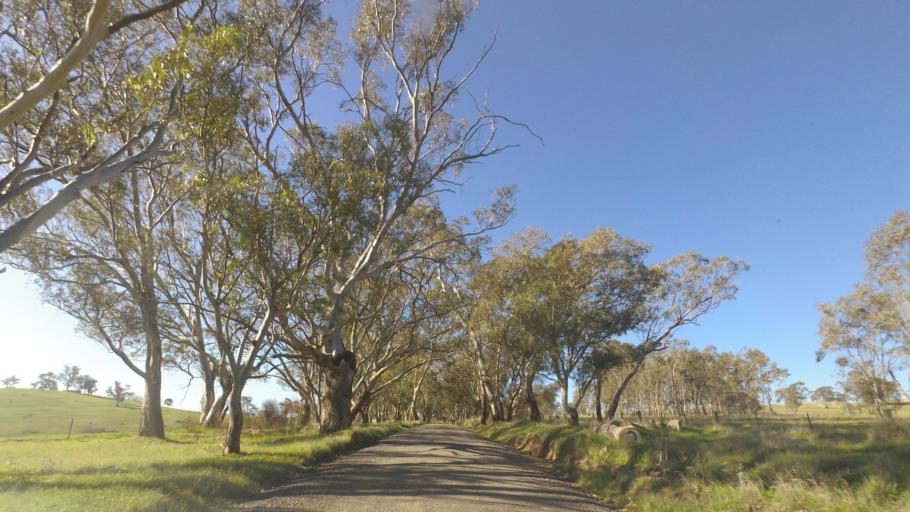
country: AU
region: Victoria
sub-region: Mount Alexander
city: Castlemaine
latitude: -36.9621
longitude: 144.3319
